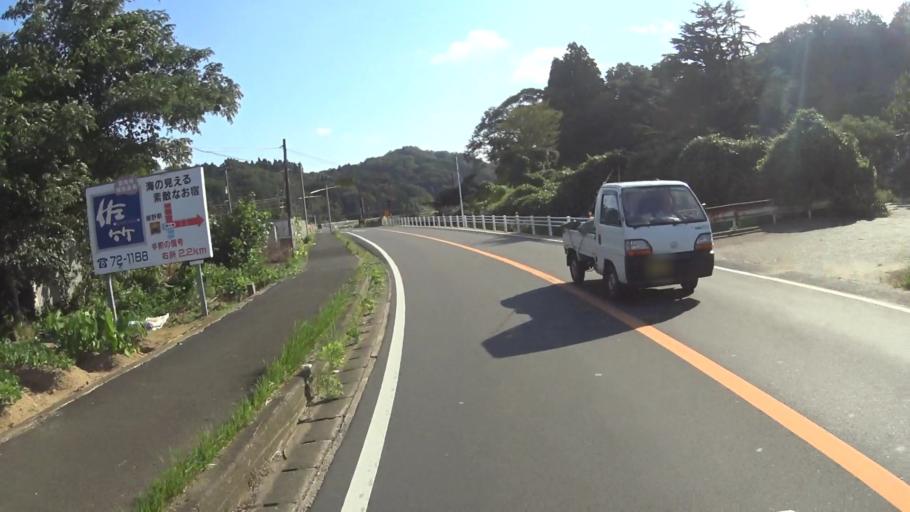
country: JP
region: Kyoto
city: Miyazu
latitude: 35.6668
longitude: 135.0238
